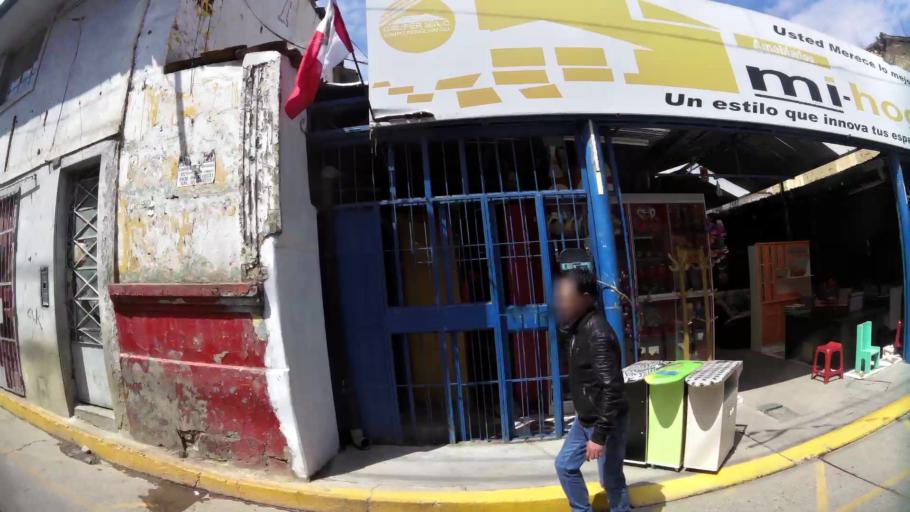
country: PE
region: Junin
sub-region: Provincia de Huancayo
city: El Tambo
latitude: -12.0717
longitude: -75.2101
